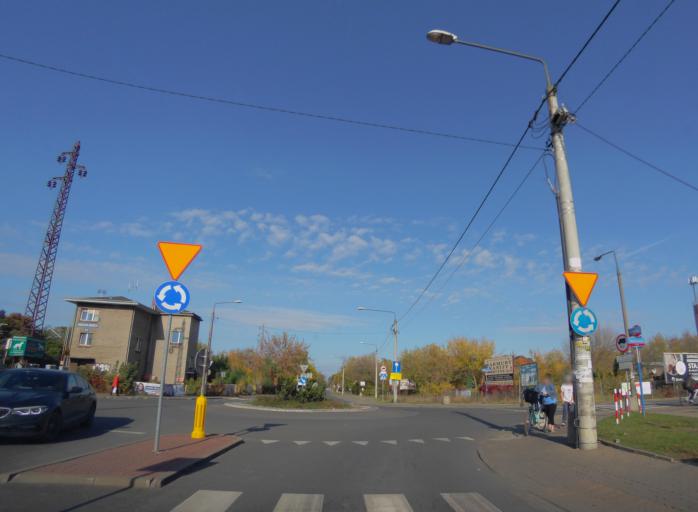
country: PL
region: Masovian Voivodeship
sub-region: Powiat otwocki
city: Jozefow
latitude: 52.1608
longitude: 21.2128
